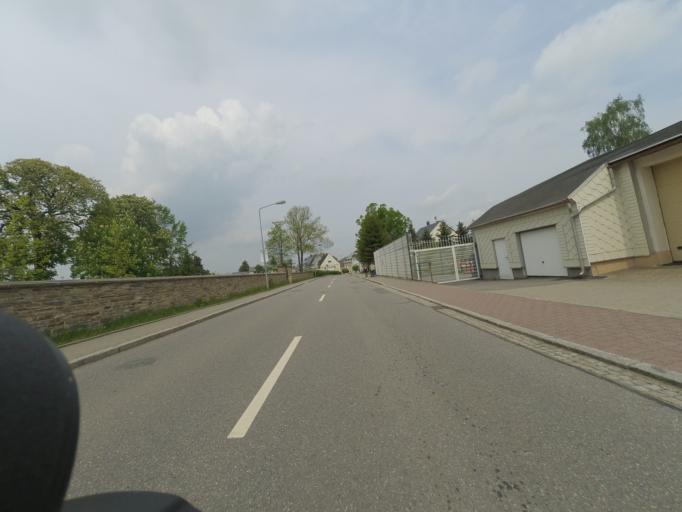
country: DE
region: Saxony
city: Zoblitz
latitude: 50.6556
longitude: 13.2364
